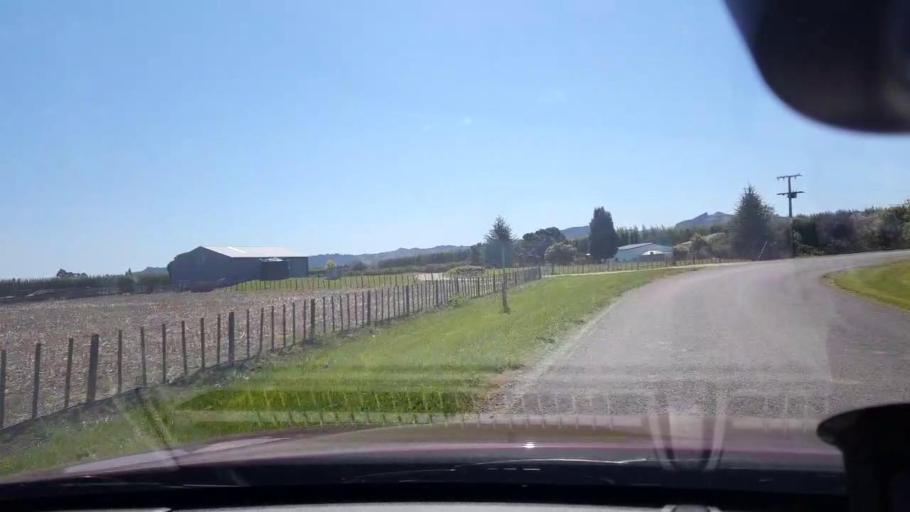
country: NZ
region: Gisborne
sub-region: Gisborne District
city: Gisborne
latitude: -38.6369
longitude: 177.9408
